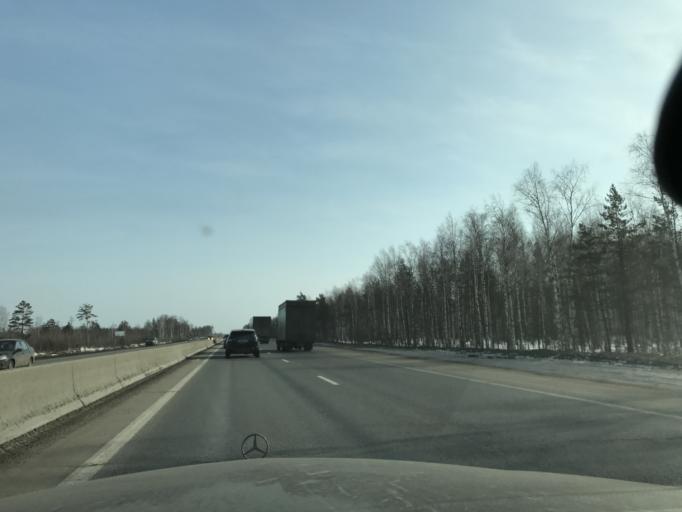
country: RU
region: Nizjnij Novgorod
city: Dzerzhinsk
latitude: 56.2988
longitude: 43.4890
